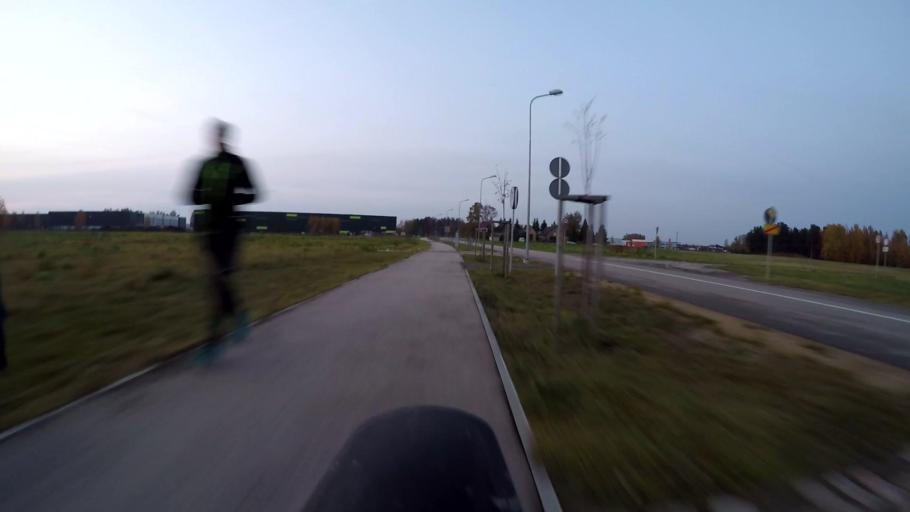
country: LV
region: Marupe
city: Marupe
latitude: 56.9152
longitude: 23.9932
